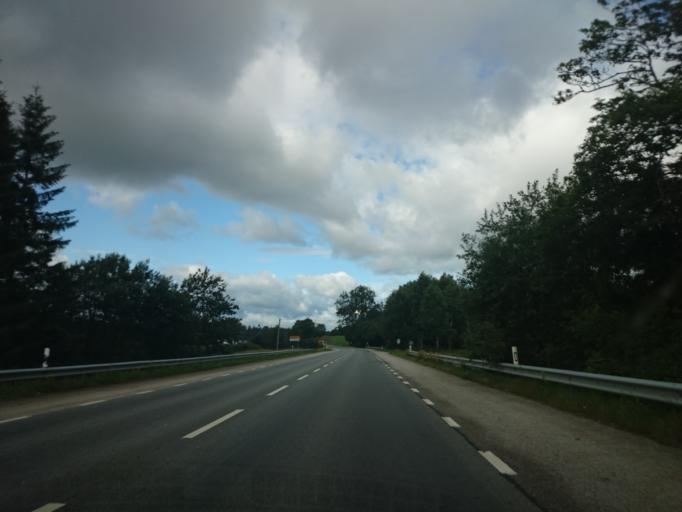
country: SE
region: Skane
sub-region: Horby Kommun
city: Hoerby
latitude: 55.9317
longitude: 13.8148
